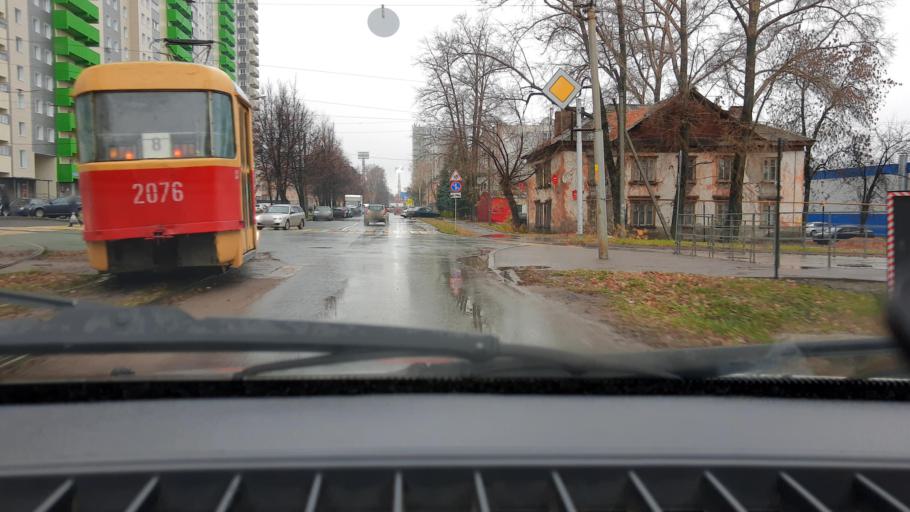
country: RU
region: Bashkortostan
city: Ufa
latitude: 54.8255
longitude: 56.0714
